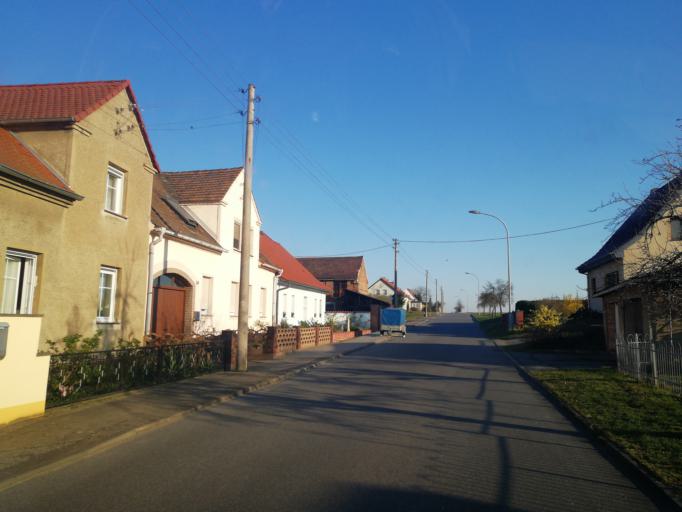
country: DE
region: Brandenburg
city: Drahnsdorf
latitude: 51.8735
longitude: 13.5858
